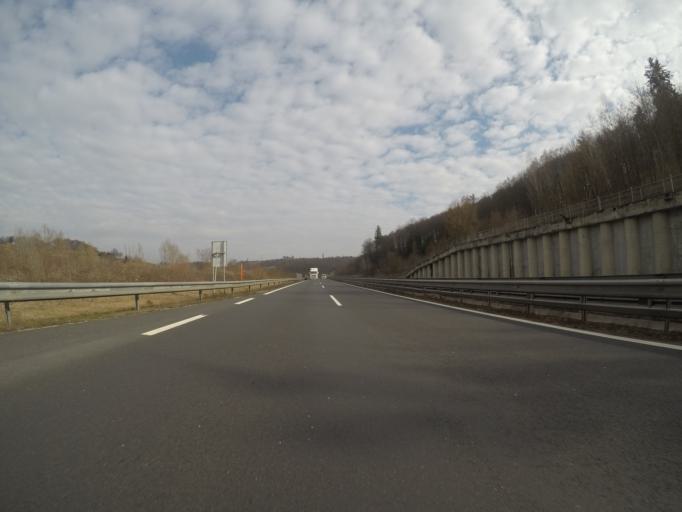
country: SI
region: Cerkvenjak
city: Cerkvenjak
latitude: 46.5808
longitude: 15.9561
